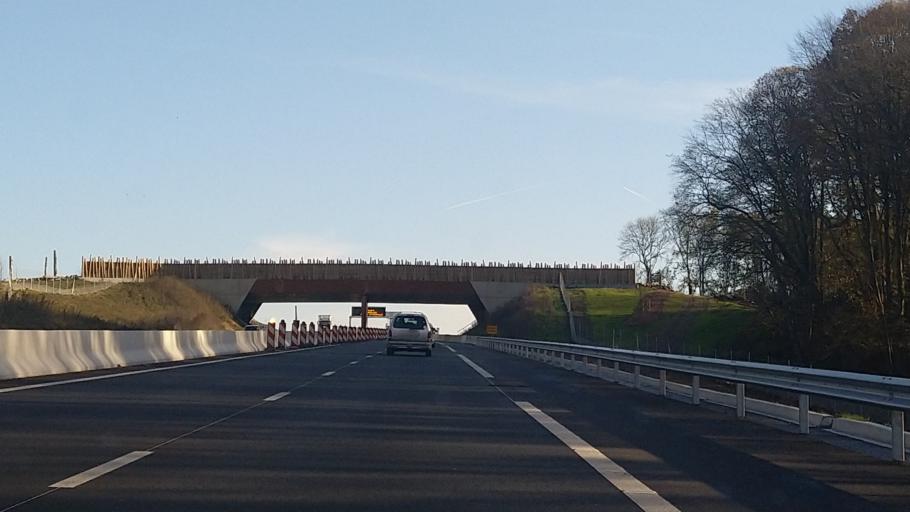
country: FR
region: Ile-de-France
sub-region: Departement du Val-d'Oise
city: Maffliers
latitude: 49.0917
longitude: 2.3051
